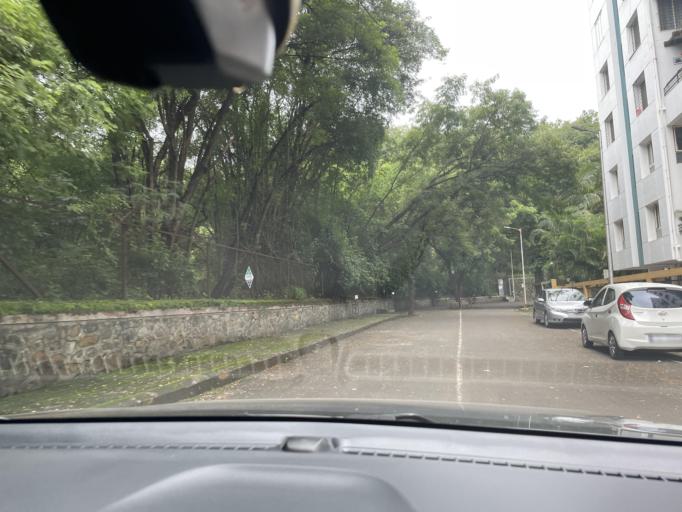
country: IN
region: Maharashtra
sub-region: Pune Division
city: Shivaji Nagar
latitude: 18.5307
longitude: 73.8149
